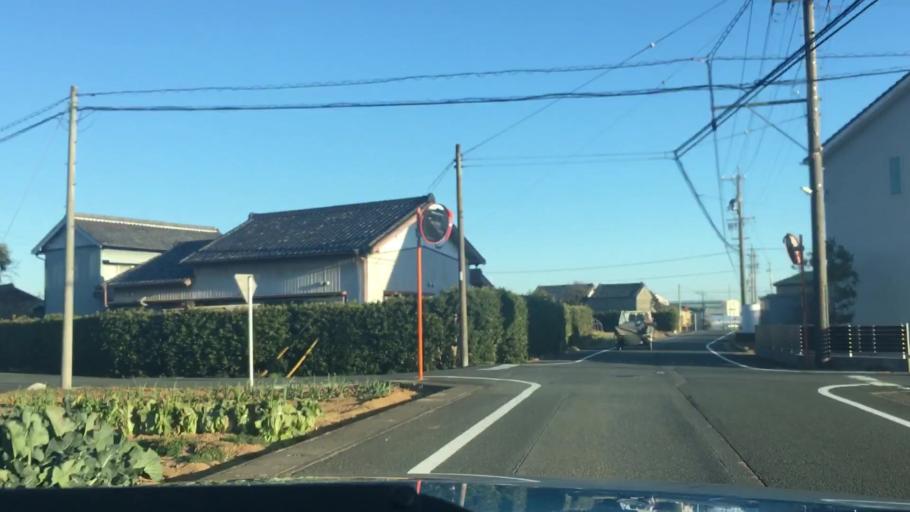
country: JP
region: Shizuoka
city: Hamamatsu
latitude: 34.7417
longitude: 137.6689
